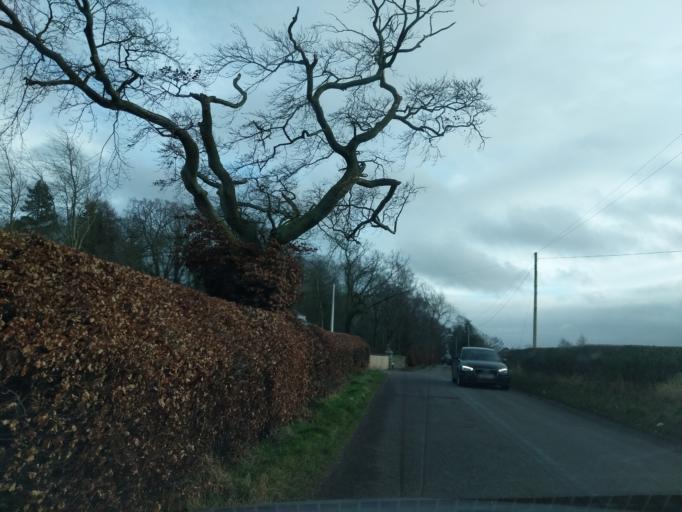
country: GB
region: Scotland
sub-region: South Lanarkshire
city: Carluke
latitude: 55.7120
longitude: -3.8503
